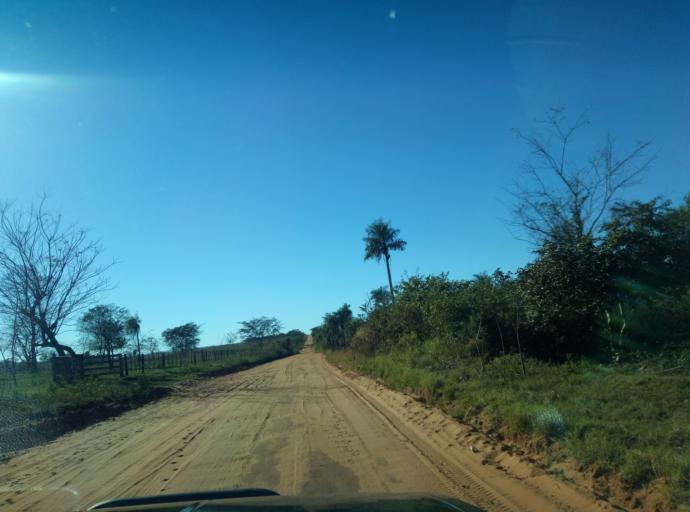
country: PY
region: Caaguazu
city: Doctor Cecilio Baez
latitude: -25.1604
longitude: -56.2808
